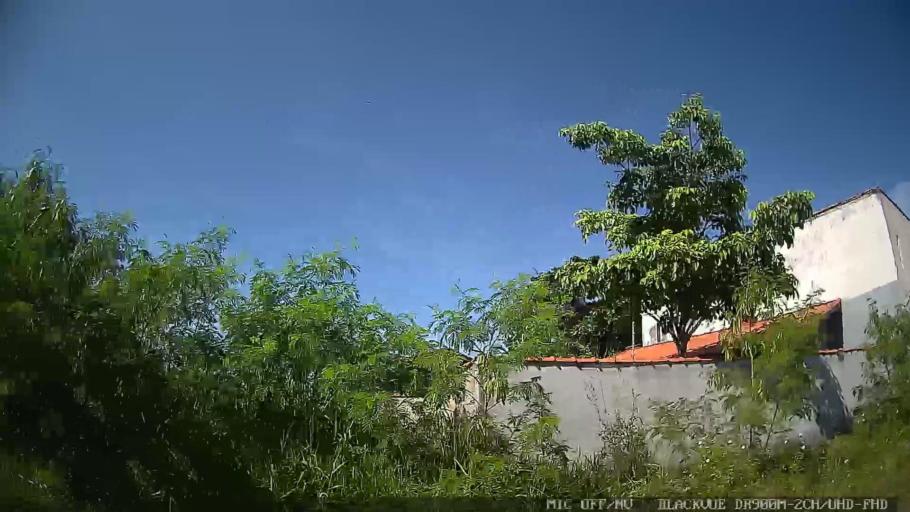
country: BR
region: Sao Paulo
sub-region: Itanhaem
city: Itanhaem
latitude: -24.2146
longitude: -46.8512
